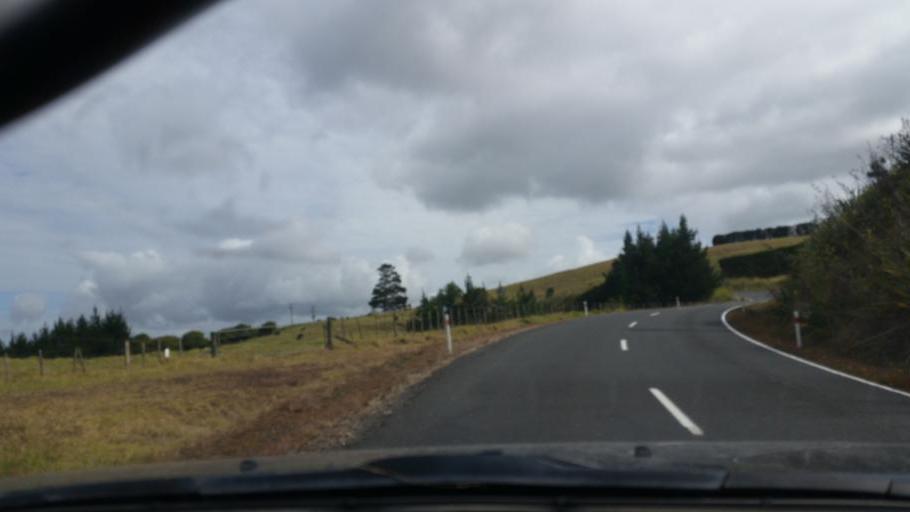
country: NZ
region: Northland
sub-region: Kaipara District
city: Dargaville
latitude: -35.9590
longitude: 173.9247
